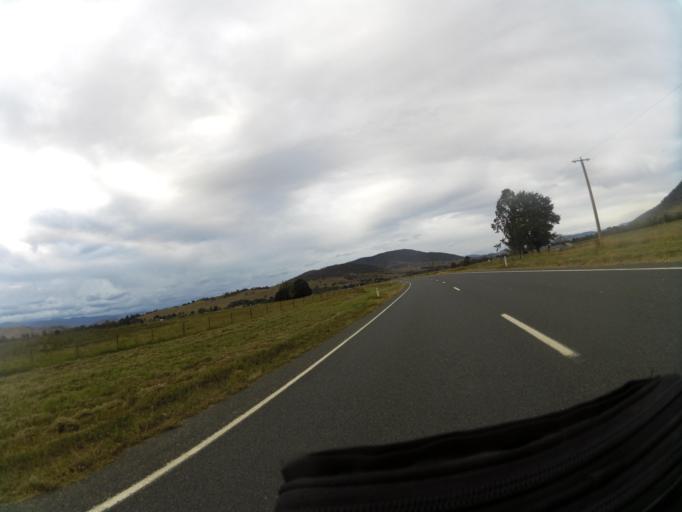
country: AU
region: New South Wales
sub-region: Snowy River
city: Jindabyne
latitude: -36.1133
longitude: 147.9794
